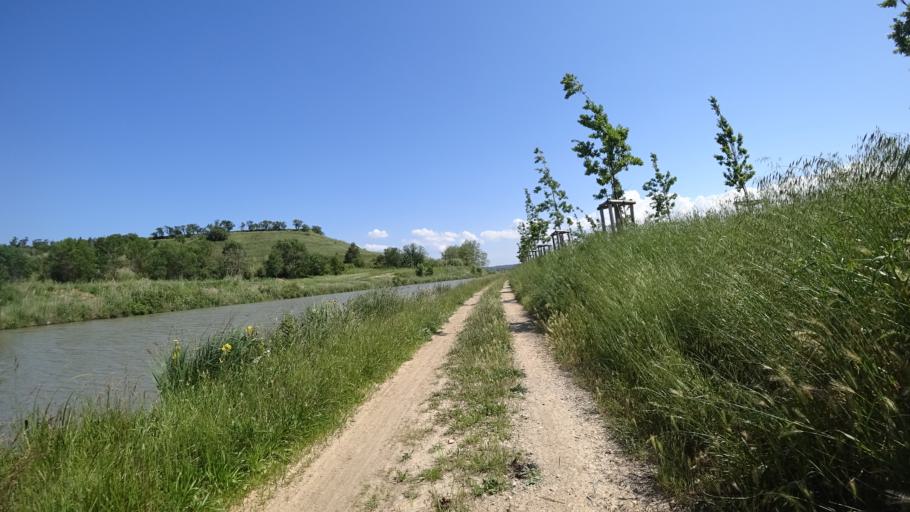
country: FR
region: Languedoc-Roussillon
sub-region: Departement de l'Aude
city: Canet
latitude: 43.2512
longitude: 2.8427
